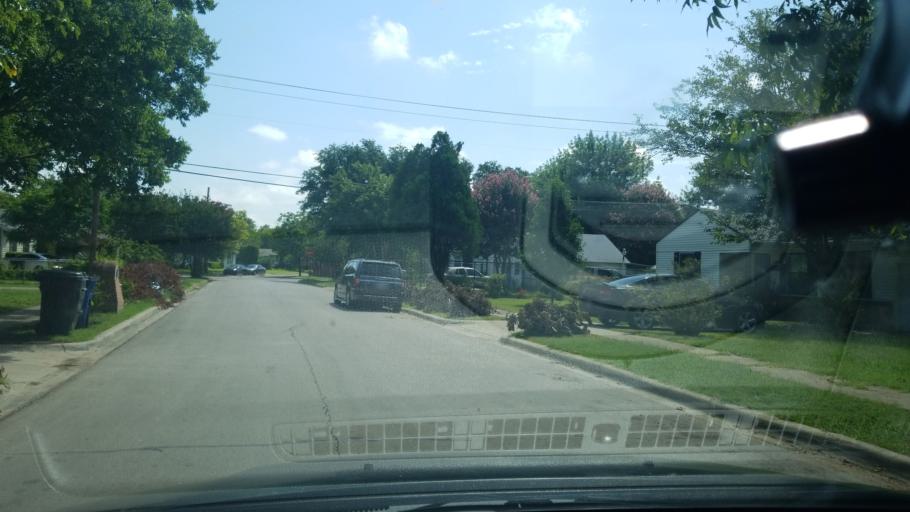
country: US
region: Texas
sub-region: Dallas County
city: Balch Springs
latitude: 32.7399
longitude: -96.6874
